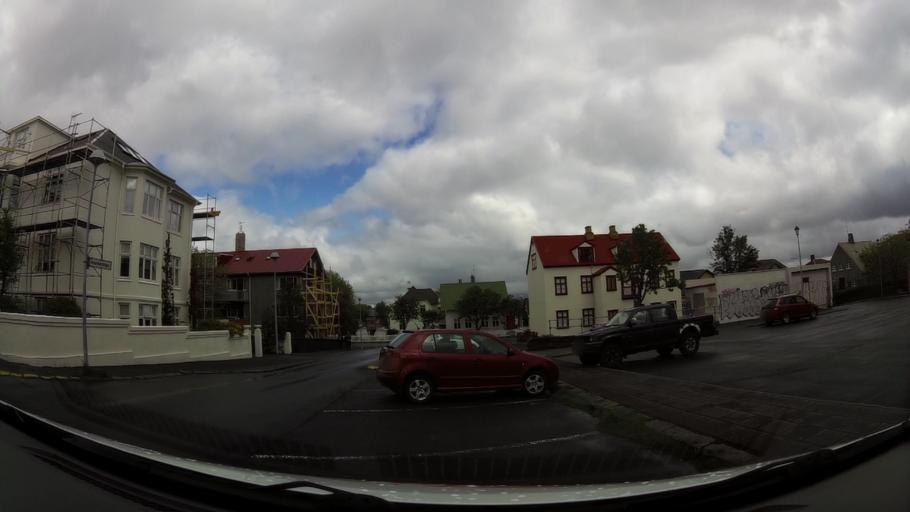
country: IS
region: Capital Region
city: Seltjarnarnes
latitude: 64.1487
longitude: -21.9499
